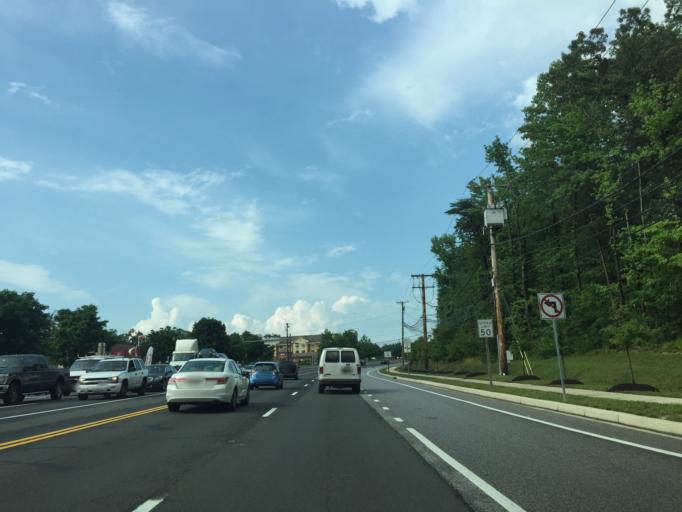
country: US
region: Maryland
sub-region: Howard County
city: Savage
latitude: 39.1450
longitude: -76.8089
